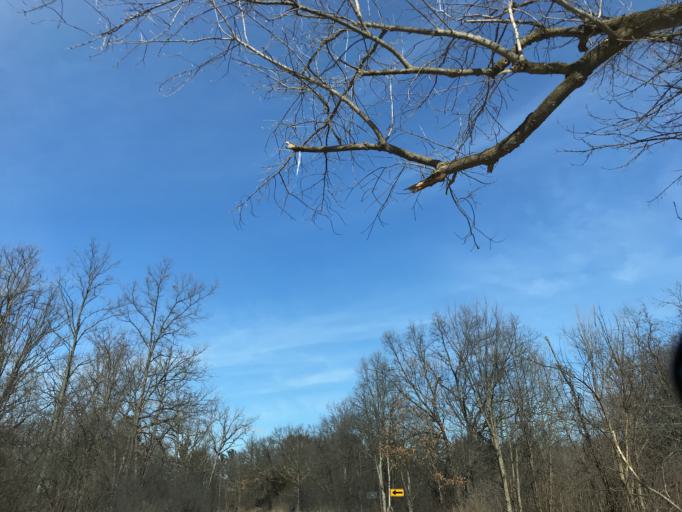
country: US
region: Michigan
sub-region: Livingston County
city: Whitmore Lake
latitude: 42.4154
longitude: -83.7394
